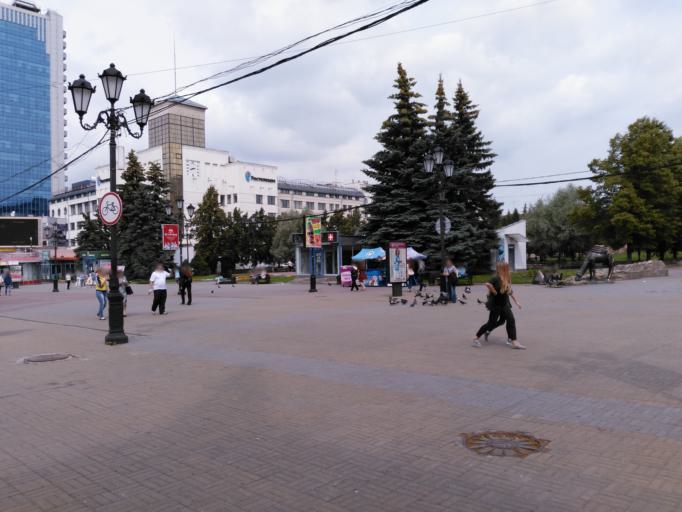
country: RU
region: Chelyabinsk
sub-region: Gorod Chelyabinsk
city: Chelyabinsk
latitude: 55.1631
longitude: 61.4006
